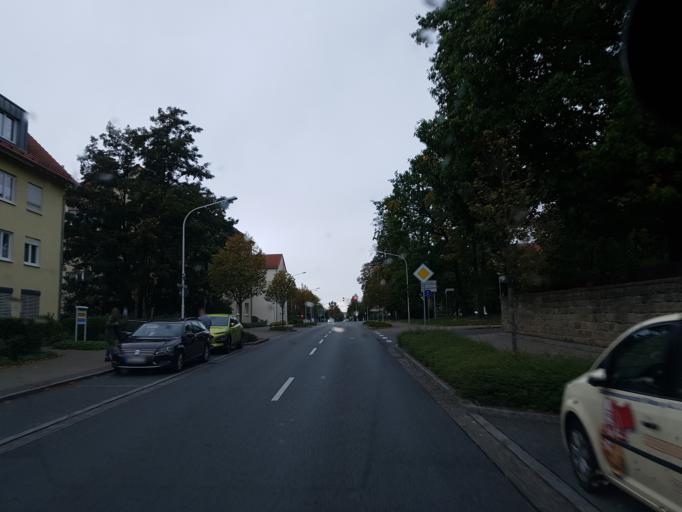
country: DE
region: Saxony
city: Riesa
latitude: 51.2995
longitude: 13.3040
